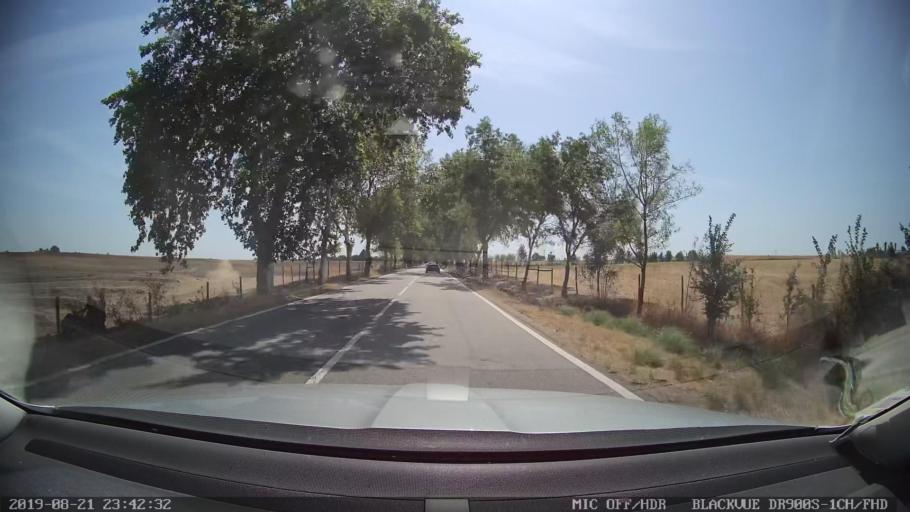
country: PT
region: Castelo Branco
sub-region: Idanha-A-Nova
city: Idanha-a-Nova
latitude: 39.8554
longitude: -7.3105
